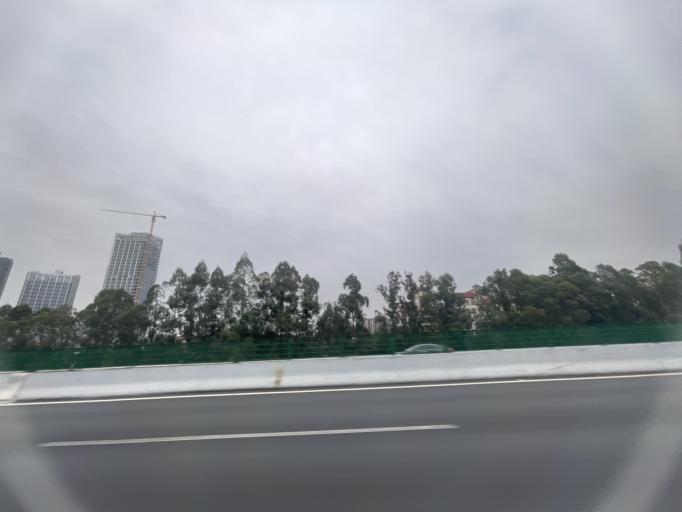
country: CN
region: Guangdong
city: Huangge
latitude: 22.7894
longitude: 113.5166
